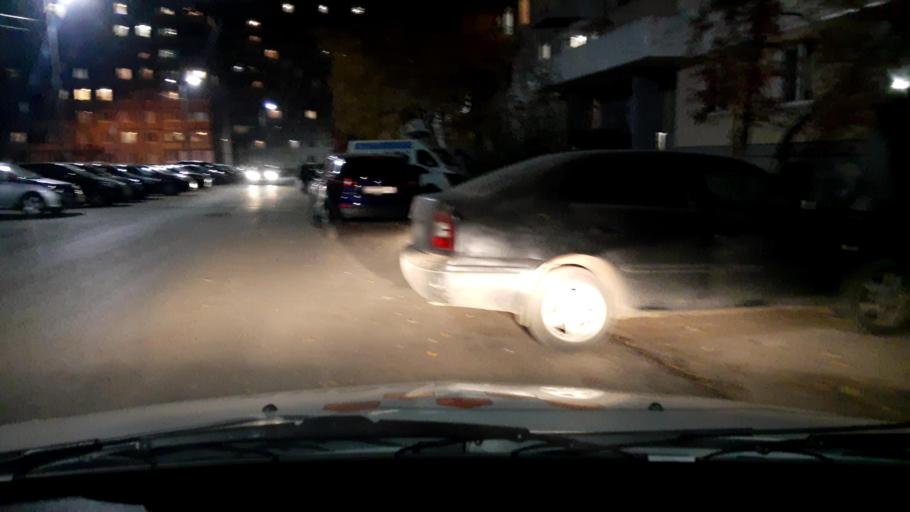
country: RU
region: Bashkortostan
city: Ufa
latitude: 54.8208
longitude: 56.1266
